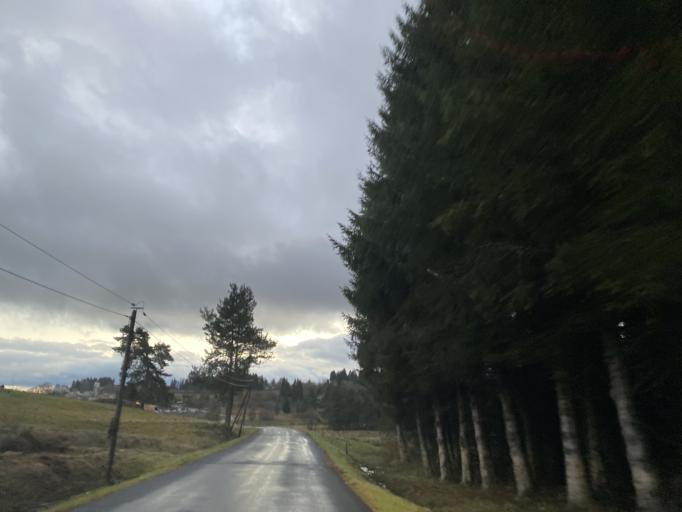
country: FR
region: Auvergne
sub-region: Departement du Puy-de-Dome
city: Cunlhat
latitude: 45.5272
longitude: 3.5870
